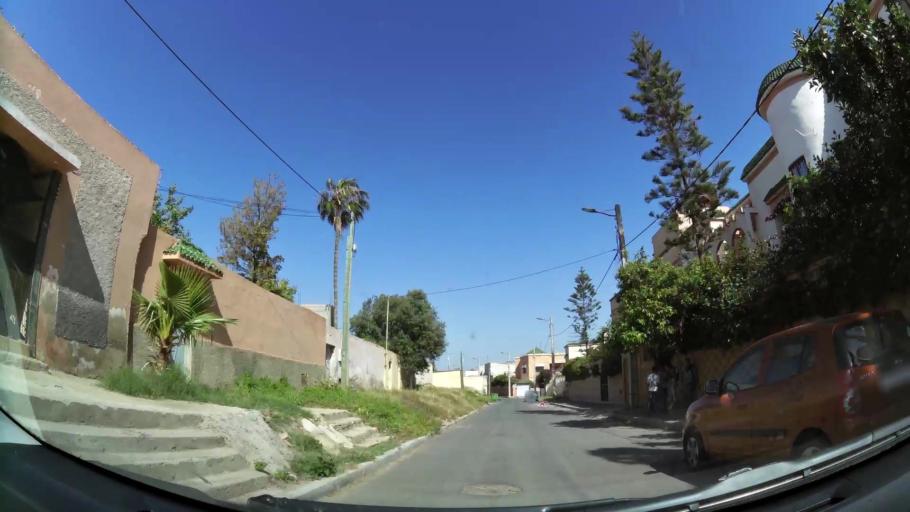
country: MA
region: Souss-Massa-Draa
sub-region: Inezgane-Ait Mellou
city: Inezgane
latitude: 30.3629
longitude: -9.5419
